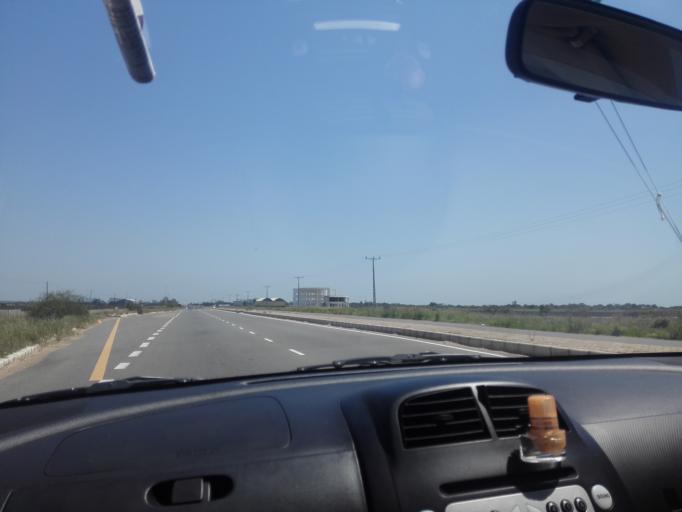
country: MZ
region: Maputo City
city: Maputo
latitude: -25.8253
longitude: 32.6722
